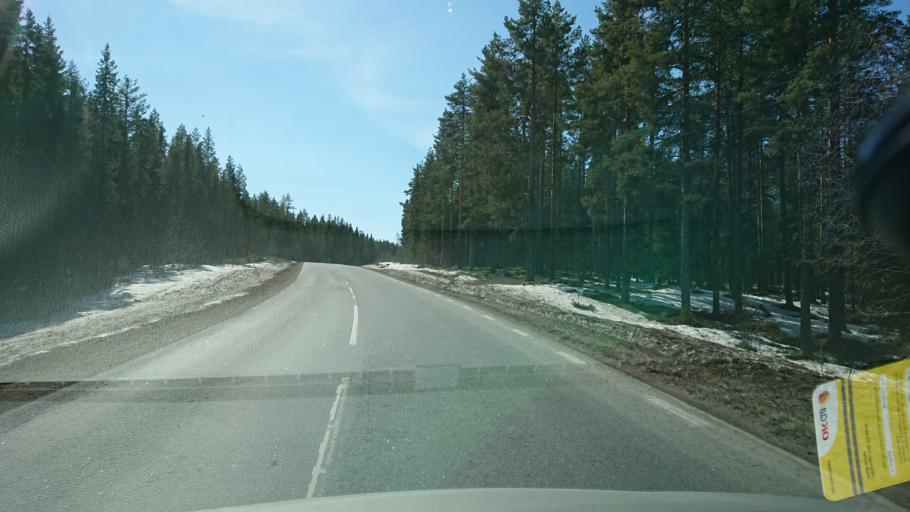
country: SE
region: Vaesternorrland
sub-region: Solleftea Kommun
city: As
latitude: 63.6284
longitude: 16.4393
